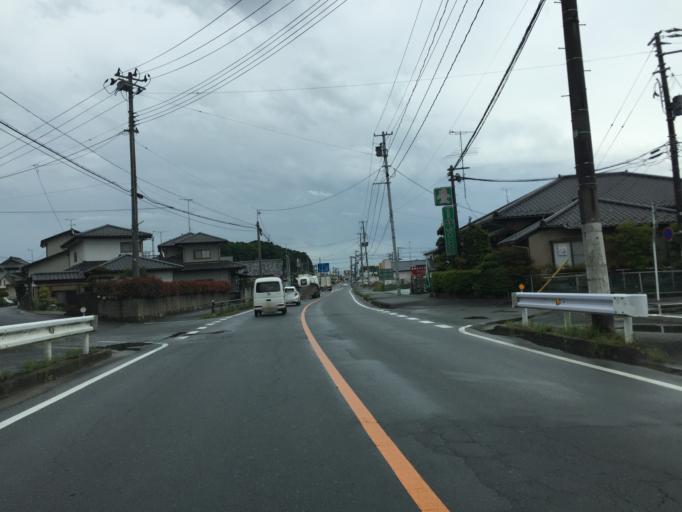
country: JP
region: Ibaraki
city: Kitaibaraki
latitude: 36.9241
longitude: 140.7837
